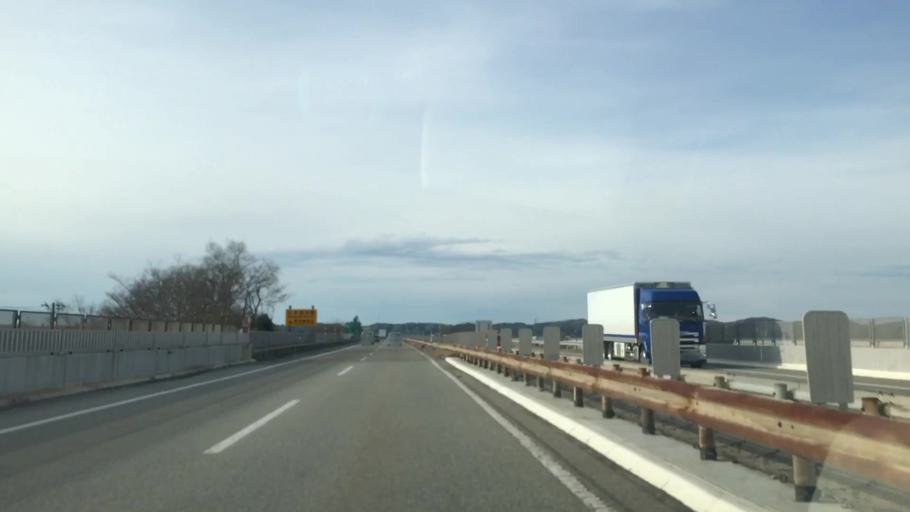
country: JP
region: Toyama
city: Toyama-shi
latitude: 36.6603
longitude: 137.1975
